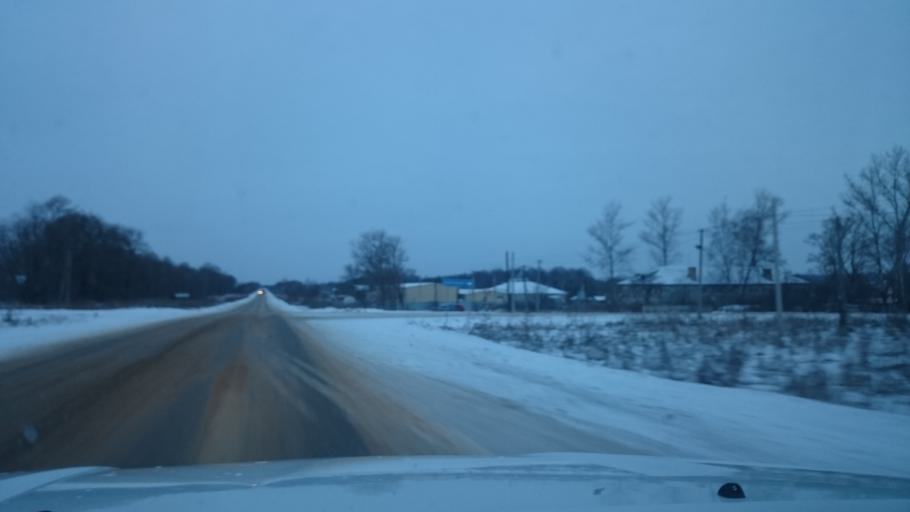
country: RU
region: Tula
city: Leninskiy
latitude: 54.2460
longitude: 37.3972
